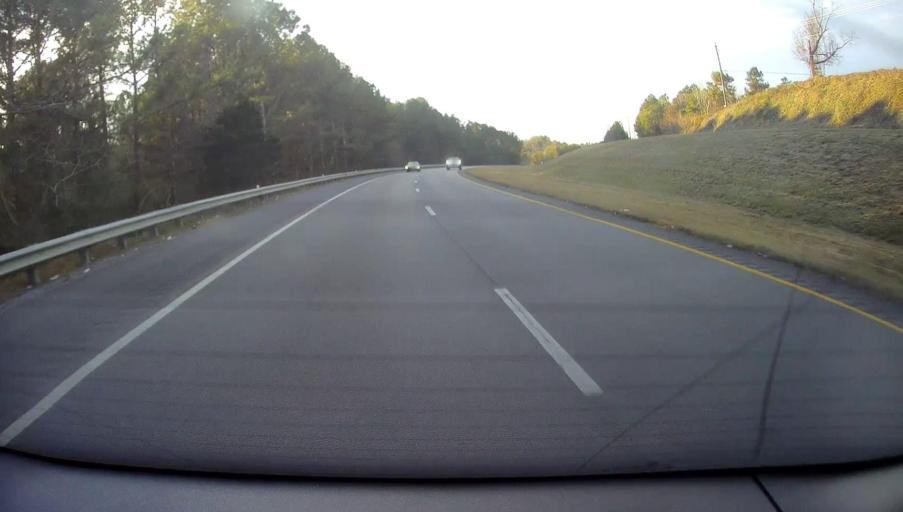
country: US
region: Alabama
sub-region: Blount County
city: Blountsville
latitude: 34.1598
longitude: -86.4966
